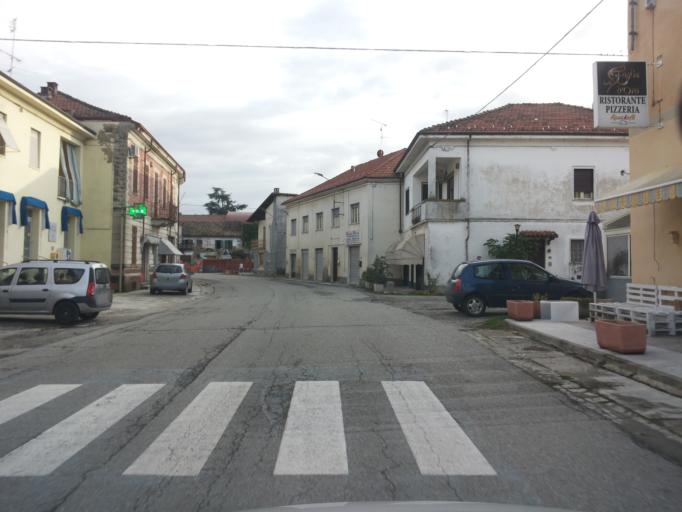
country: IT
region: Piedmont
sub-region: Provincia di Alessandria
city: Cereseto
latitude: 45.1032
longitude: 8.3070
